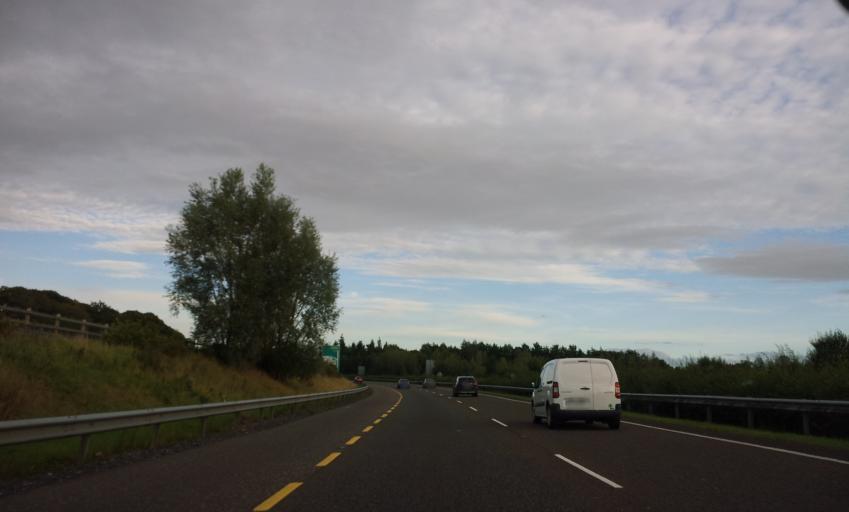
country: IE
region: Munster
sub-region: An Clar
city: Shannon
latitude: 52.7199
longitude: -8.8565
